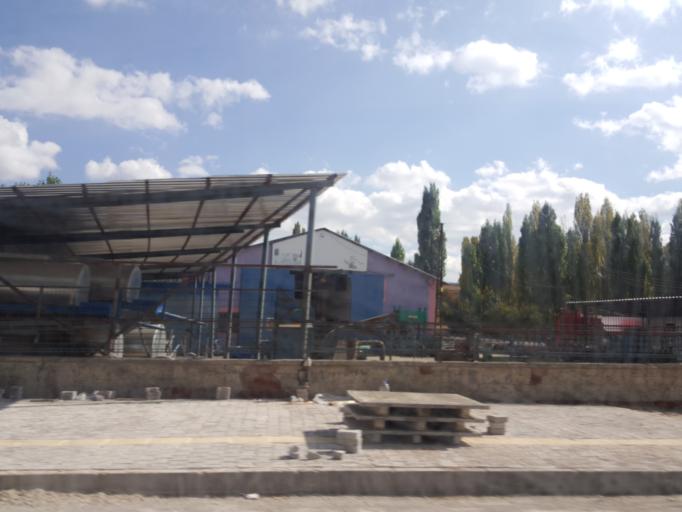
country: TR
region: Tokat
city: Artova
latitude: 40.1153
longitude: 36.3099
